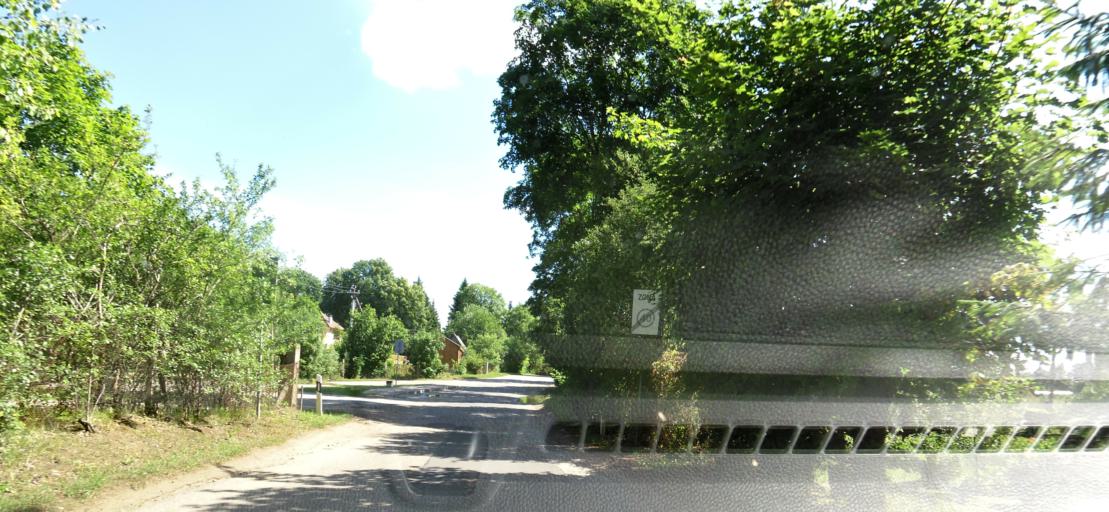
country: LT
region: Vilnius County
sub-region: Vilnius
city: Fabijoniskes
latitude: 54.8155
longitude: 25.3217
